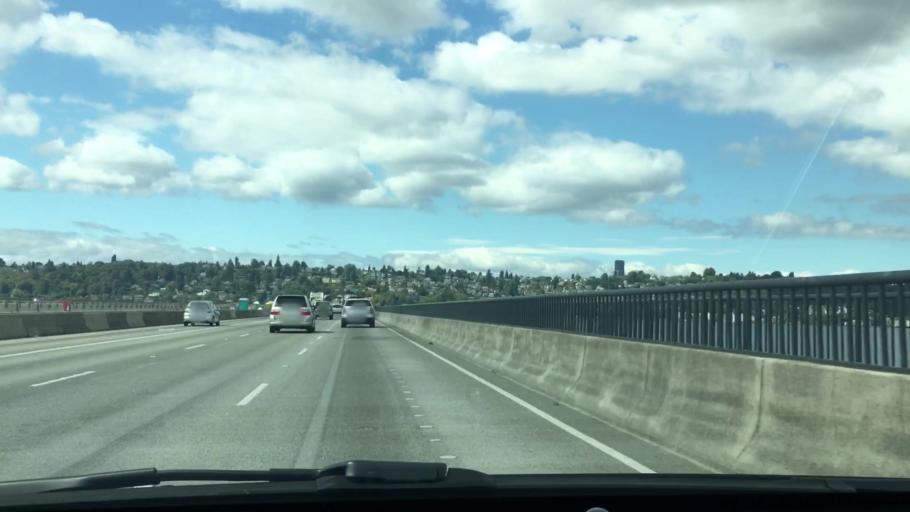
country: US
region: Washington
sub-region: King County
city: Mercer Island
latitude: 47.5903
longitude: -122.2665
